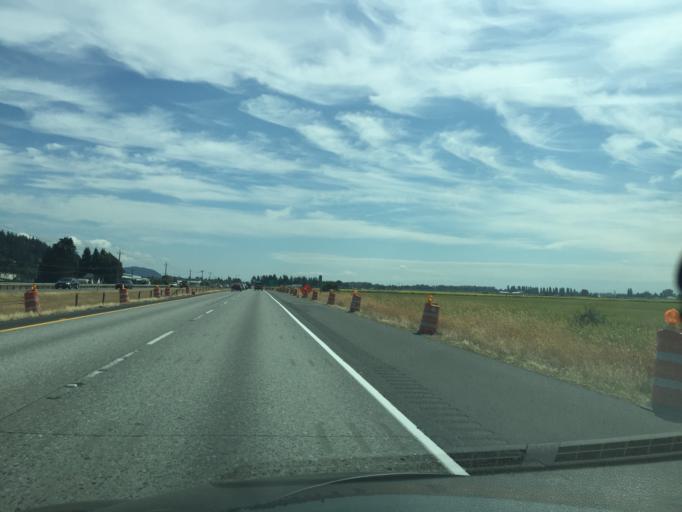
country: US
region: Washington
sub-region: Skagit County
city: Burlington
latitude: 48.4969
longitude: -122.3356
